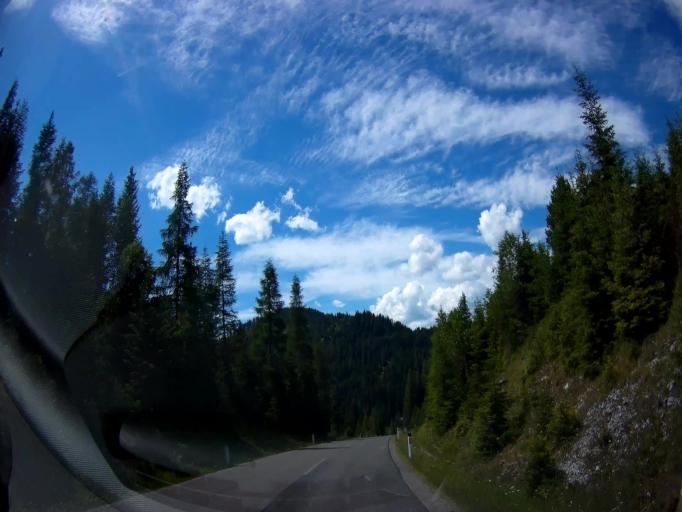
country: AT
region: Carinthia
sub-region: Politischer Bezirk Sankt Veit an der Glan
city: Glodnitz
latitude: 46.9473
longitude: 14.0272
